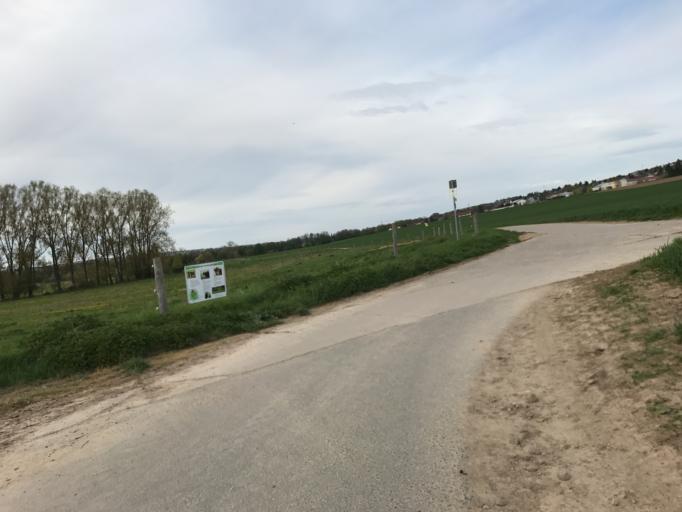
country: DE
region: Rheinland-Pfalz
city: Sorgenloch
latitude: 49.8897
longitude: 8.1925
